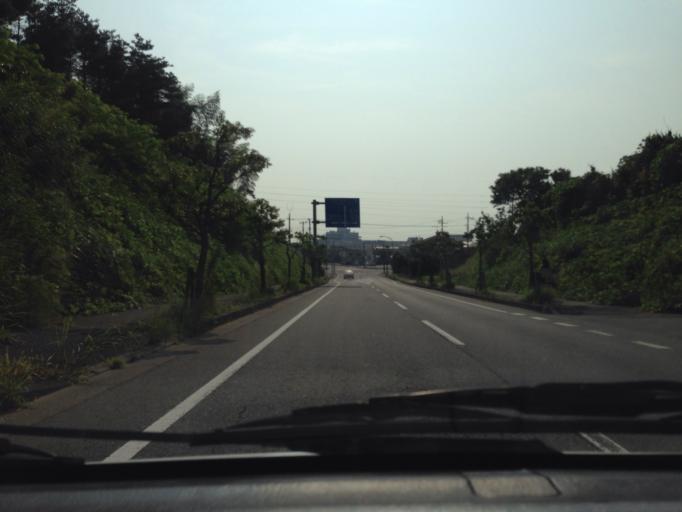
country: JP
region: Ibaraki
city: Ami
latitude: 36.0583
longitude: 140.2126
